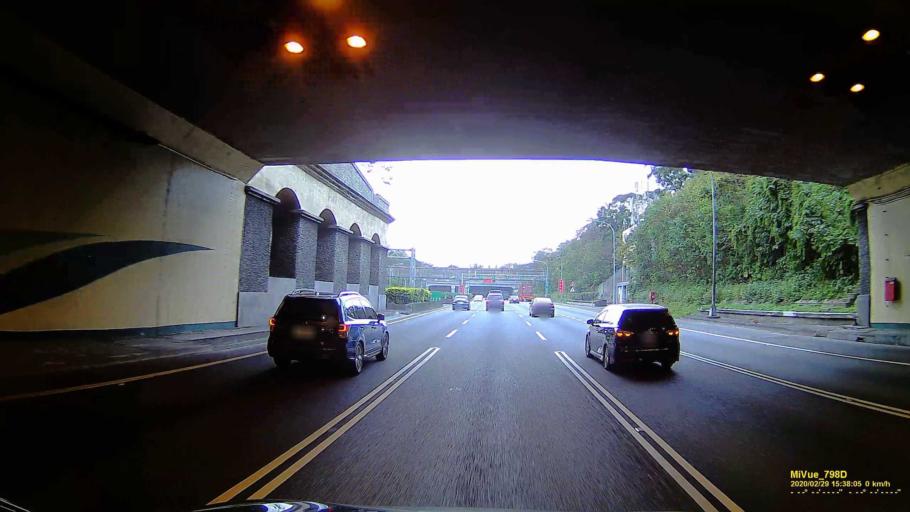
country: TW
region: Taiwan
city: Daxi
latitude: 24.9068
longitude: 121.2836
